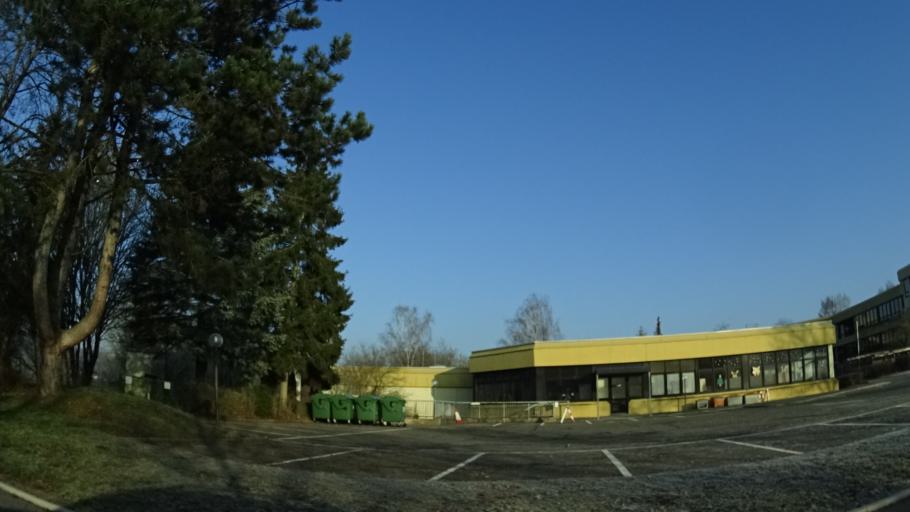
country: DE
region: Bavaria
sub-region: Upper Franconia
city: Coburg
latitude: 50.2591
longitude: 10.9452
